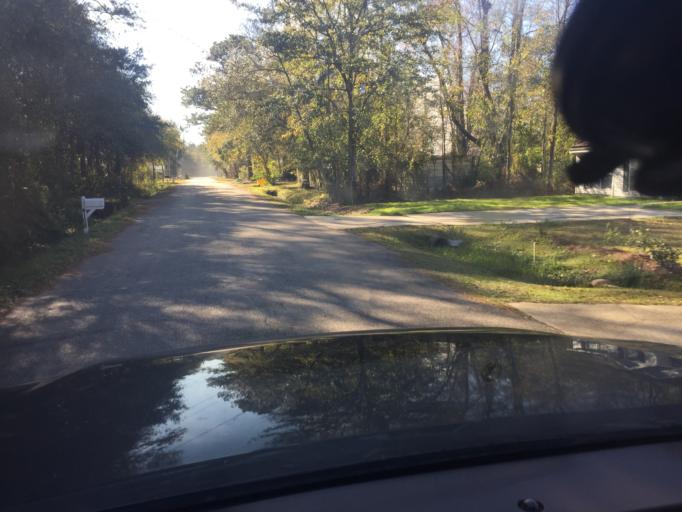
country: US
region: Louisiana
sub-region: Saint Tammany Parish
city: Slidell
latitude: 30.3126
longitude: -89.7365
